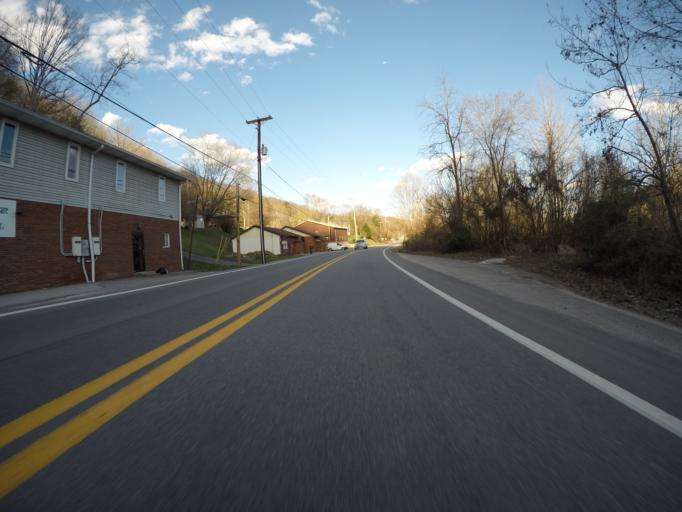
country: US
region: West Virginia
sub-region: Kanawha County
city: Charleston
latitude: 38.4004
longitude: -81.5815
